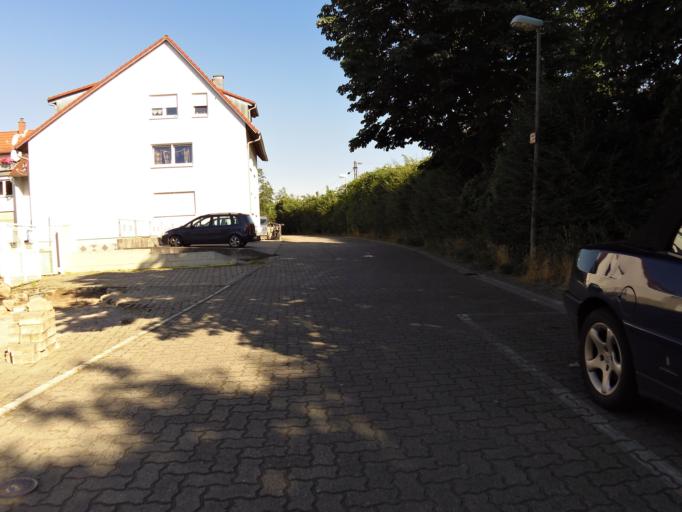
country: DE
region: Rheinland-Pfalz
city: Frankenthal
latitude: 49.4978
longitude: 8.3688
